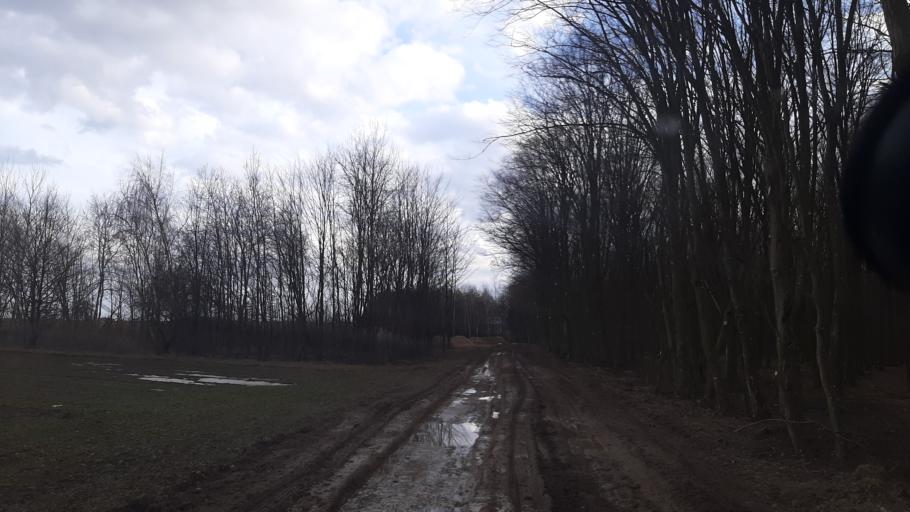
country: PL
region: Lublin Voivodeship
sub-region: Powiat lubelski
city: Jastkow
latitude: 51.3713
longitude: 22.4168
